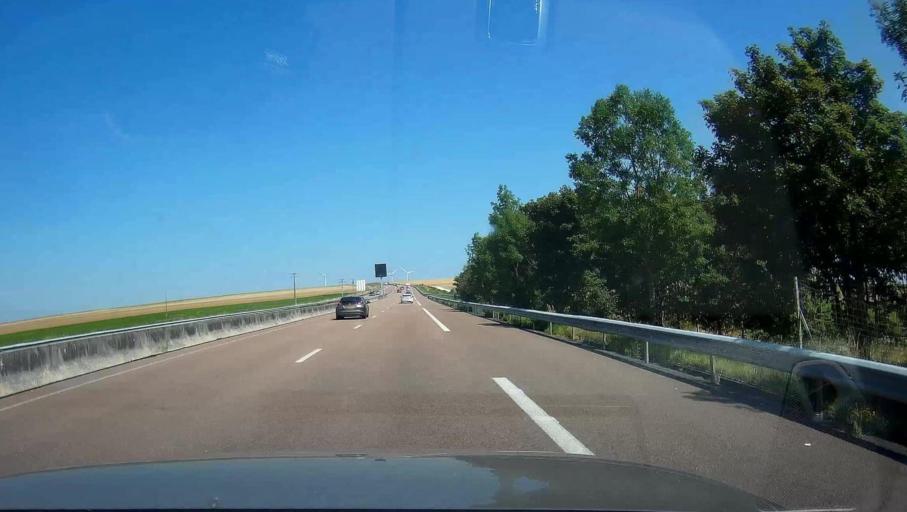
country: FR
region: Champagne-Ardenne
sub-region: Departement de l'Aube
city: Creney-pres-Troyes
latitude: 48.4311
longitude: 4.1511
